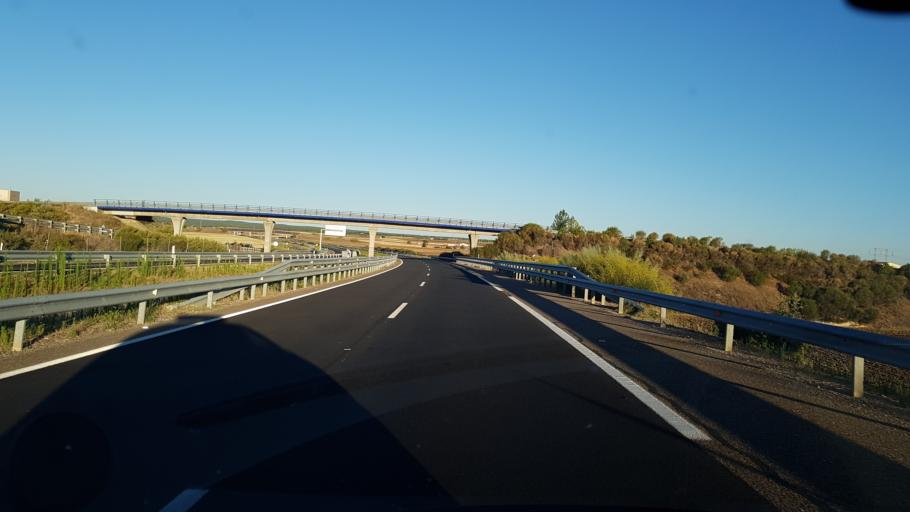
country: ES
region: Castille and Leon
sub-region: Provincia de Zamora
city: Toro
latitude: 41.5480
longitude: -5.3896
